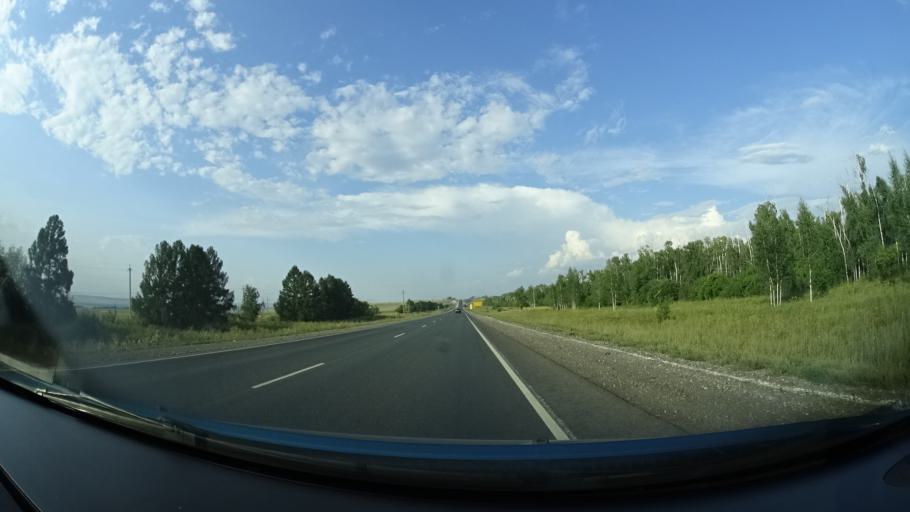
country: RU
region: Samara
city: Sukhodol
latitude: 53.7207
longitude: 50.8276
